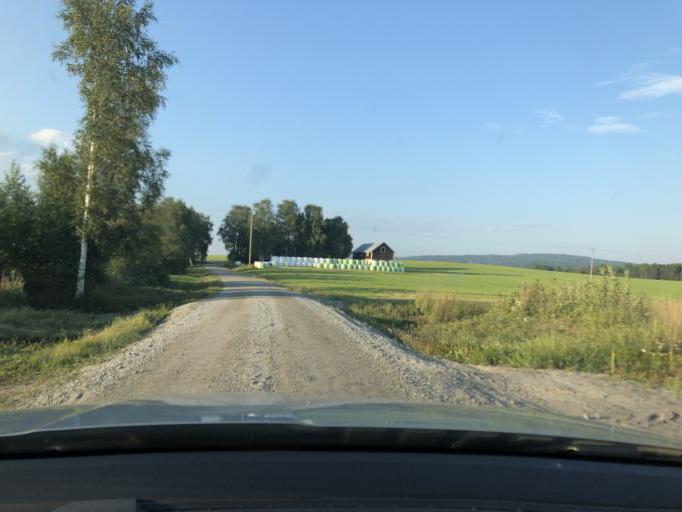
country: SE
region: Vaesternorrland
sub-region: Kramfors Kommun
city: Bollstabruk
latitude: 63.0722
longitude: 17.7355
